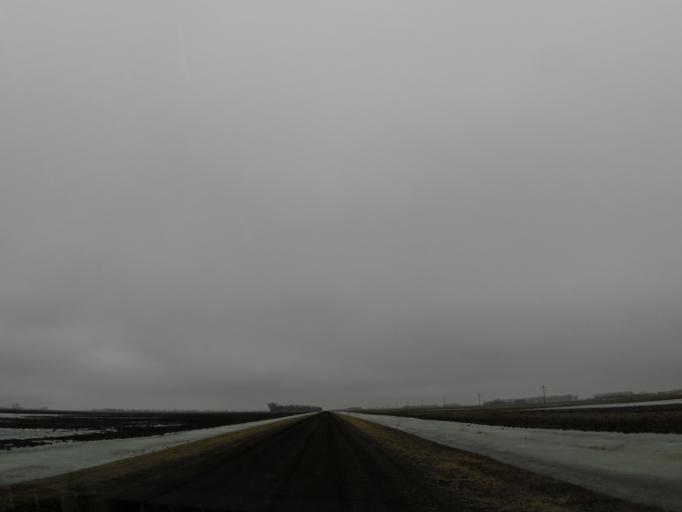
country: US
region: North Dakota
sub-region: Walsh County
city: Grafton
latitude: 48.3981
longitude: -97.2338
